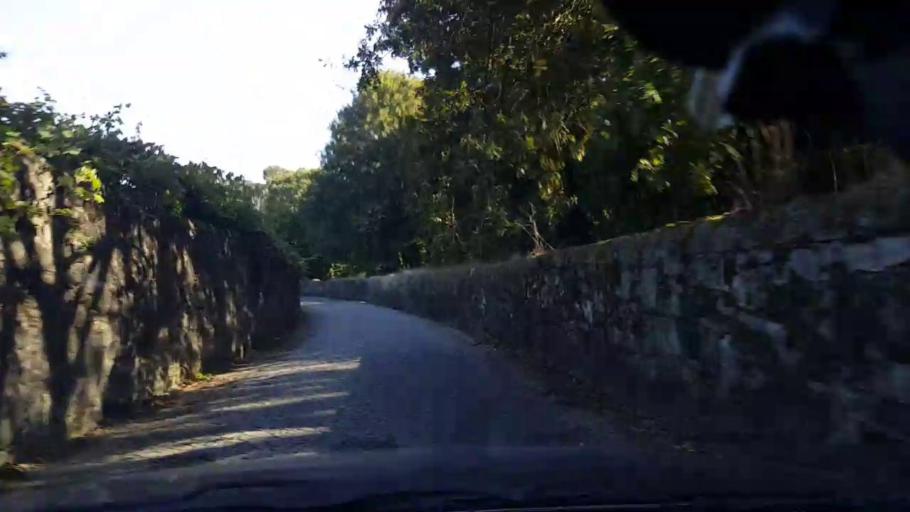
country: PT
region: Porto
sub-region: Vila do Conde
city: Arvore
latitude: 41.3417
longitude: -8.6865
